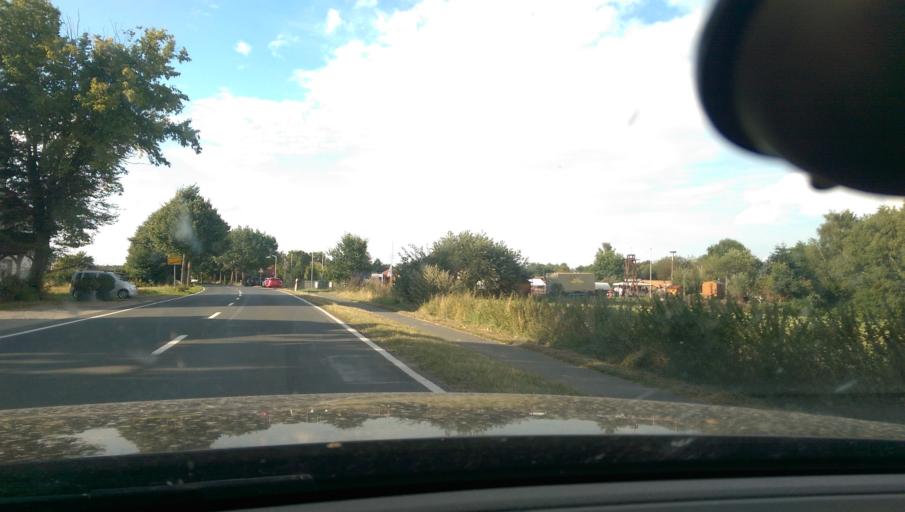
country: DE
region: Lower Saxony
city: Neustadt am Rubenberge
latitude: 52.5142
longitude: 9.4525
